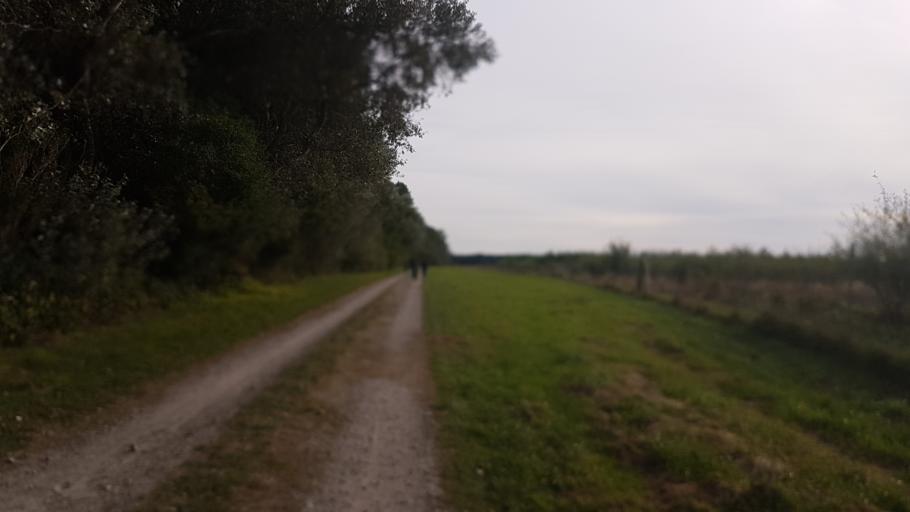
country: DE
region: Mecklenburg-Vorpommern
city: Hiddensee
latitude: 54.4869
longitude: 13.1620
